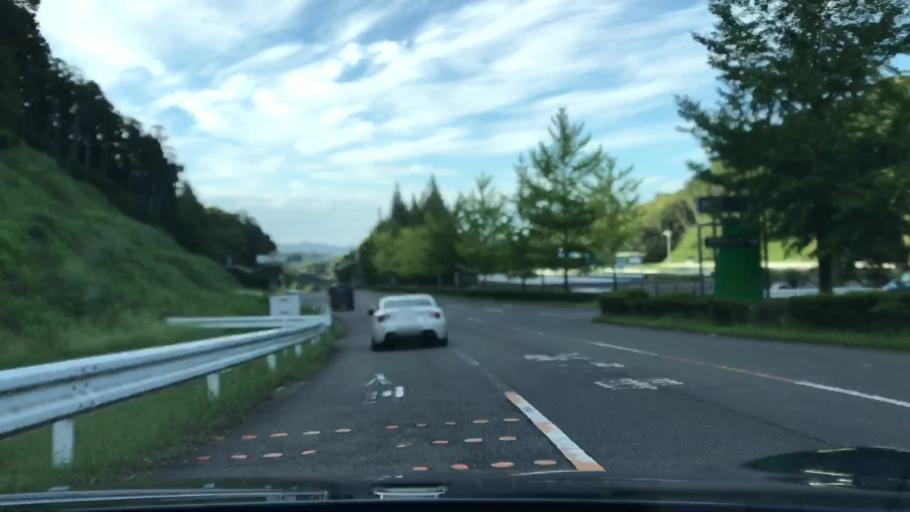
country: JP
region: Tochigi
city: Motegi
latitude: 36.5398
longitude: 140.2306
